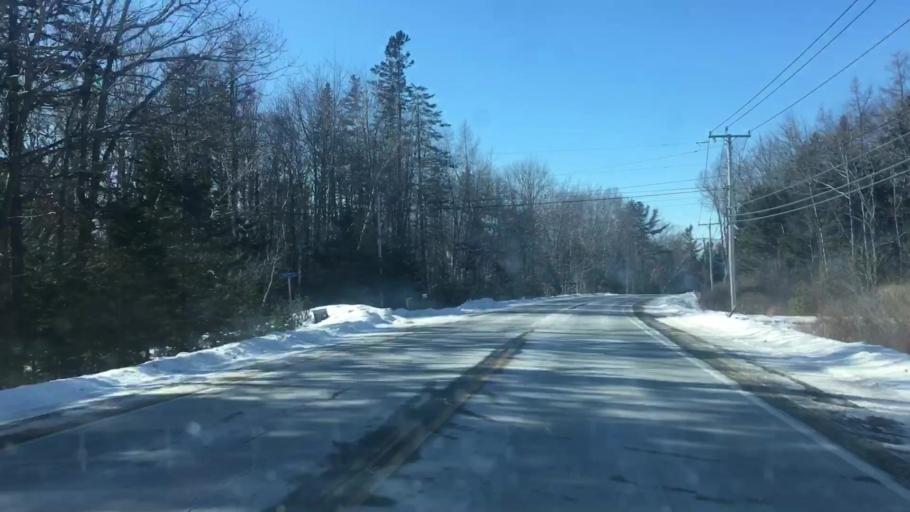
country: US
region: Maine
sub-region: Hancock County
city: Surry
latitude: 44.4928
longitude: -68.4580
